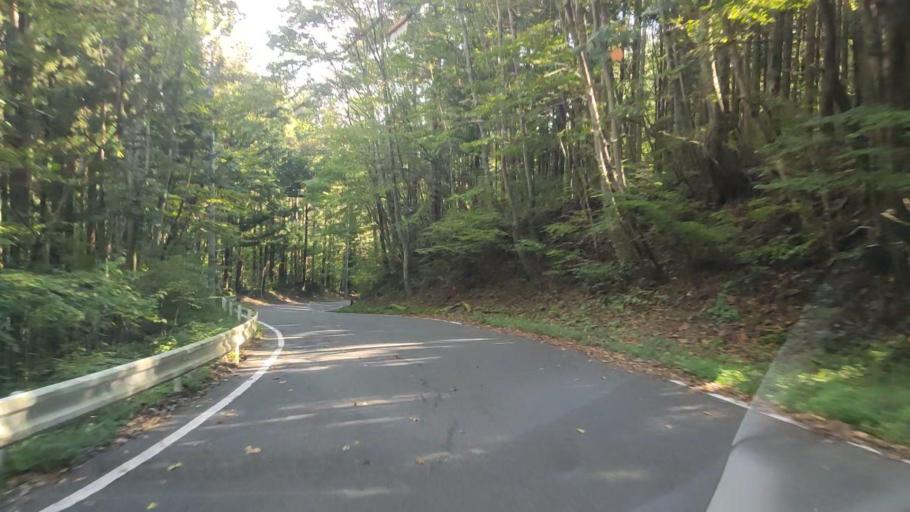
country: JP
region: Gunma
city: Nakanojomachi
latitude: 36.5976
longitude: 138.6969
